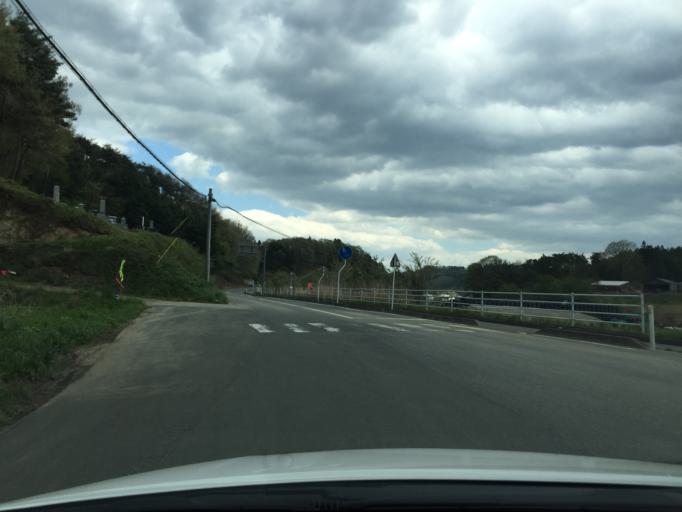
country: JP
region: Fukushima
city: Yanagawamachi-saiwaicho
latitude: 37.7010
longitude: 140.7494
